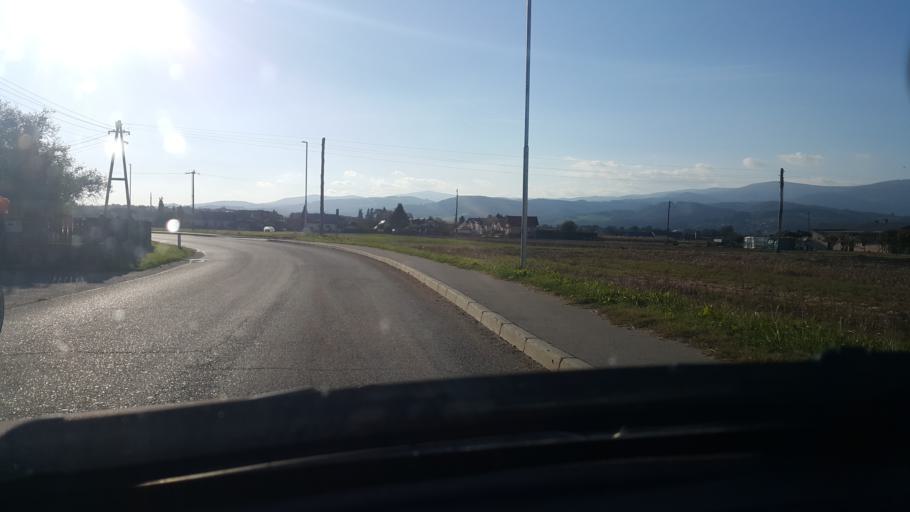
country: SI
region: Race-Fram
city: Race
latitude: 46.4534
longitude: 15.6907
